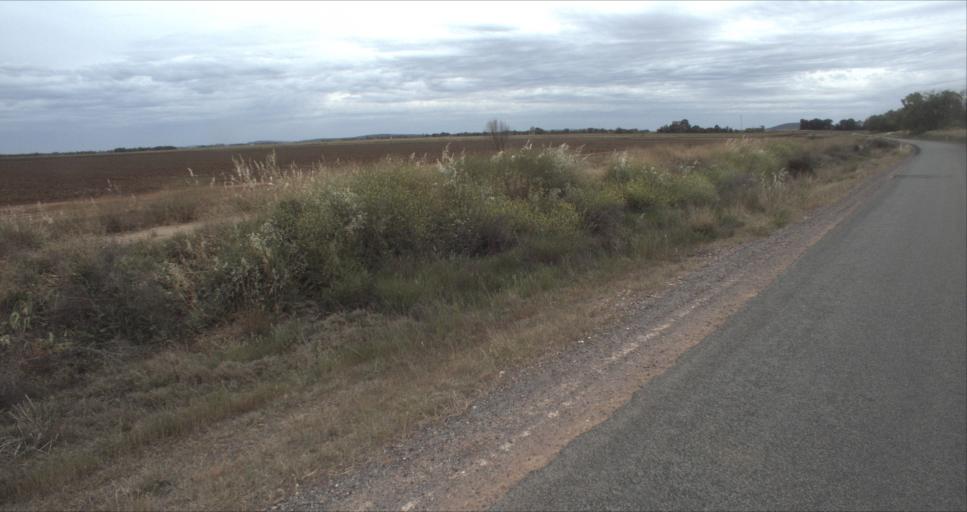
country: AU
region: New South Wales
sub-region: Leeton
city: Leeton
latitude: -34.4303
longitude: 146.3776
